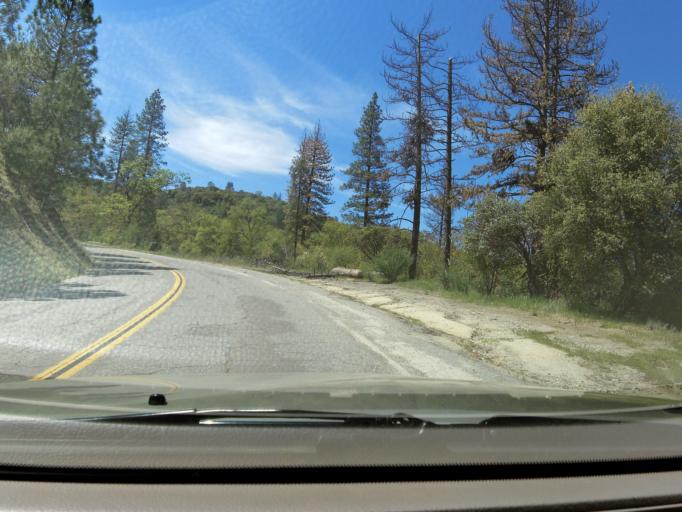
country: US
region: California
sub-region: Fresno County
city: Auberry
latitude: 37.2303
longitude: -119.5107
